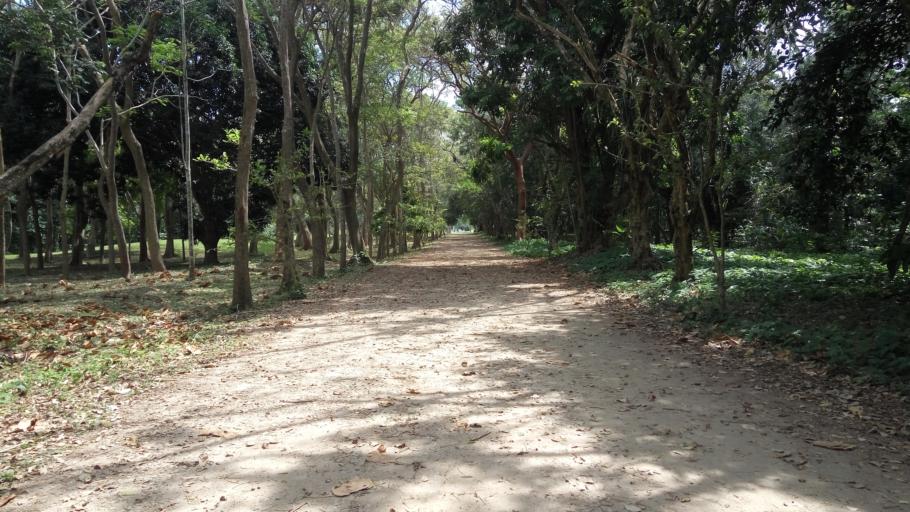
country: MX
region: Tabasco
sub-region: Comalcalco
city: Oriente 1ra. Seccion (Santo Domingo)
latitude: 18.2799
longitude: -93.2043
